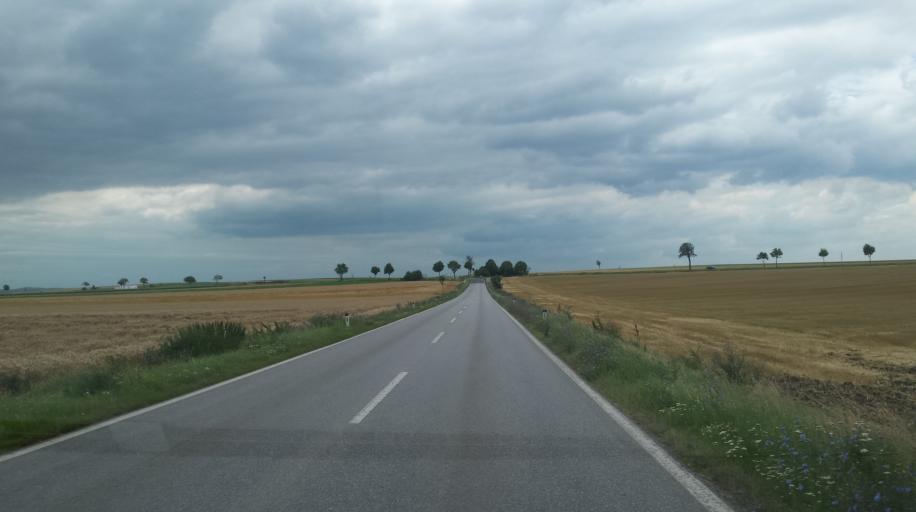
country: AT
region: Lower Austria
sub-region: Politischer Bezirk Wien-Umgebung
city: Moosbrunn
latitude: 48.0468
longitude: 16.4626
